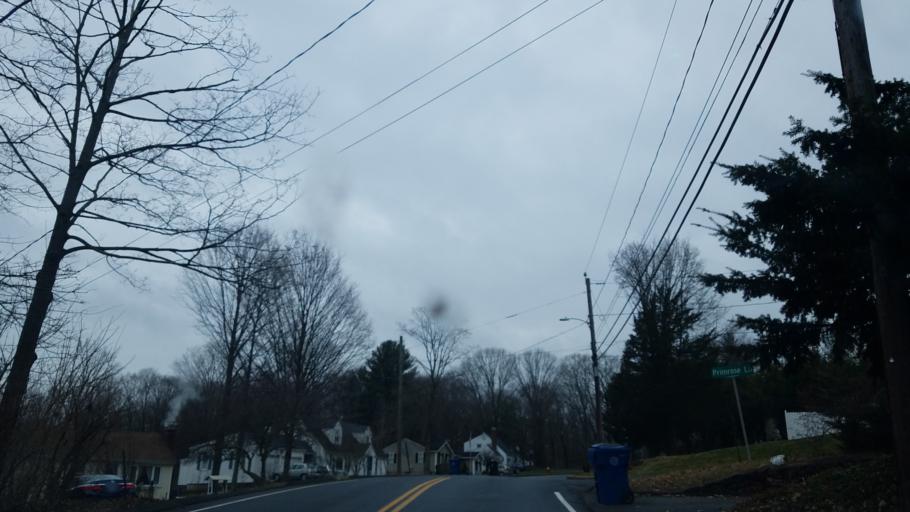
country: US
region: Connecticut
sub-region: Hartford County
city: Kensington
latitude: 41.6250
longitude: -72.7727
